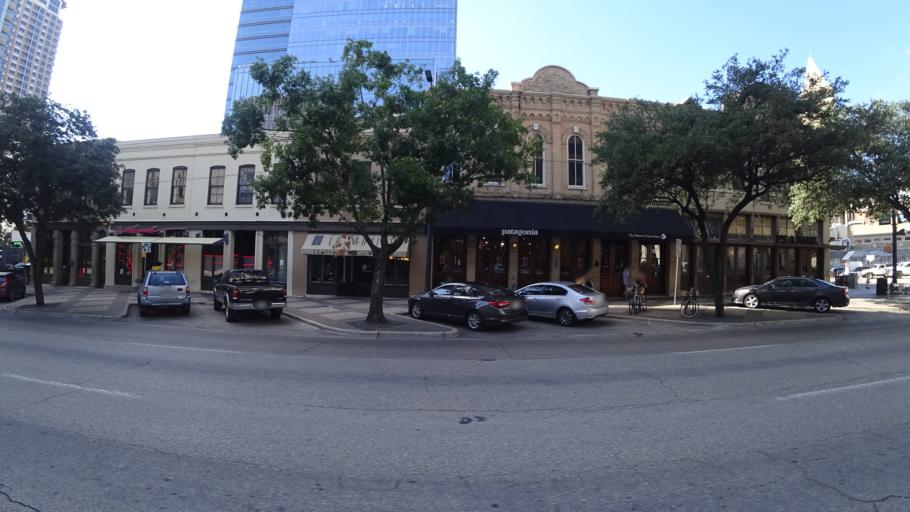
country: US
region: Texas
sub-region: Travis County
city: Austin
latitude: 30.2659
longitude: -97.7437
